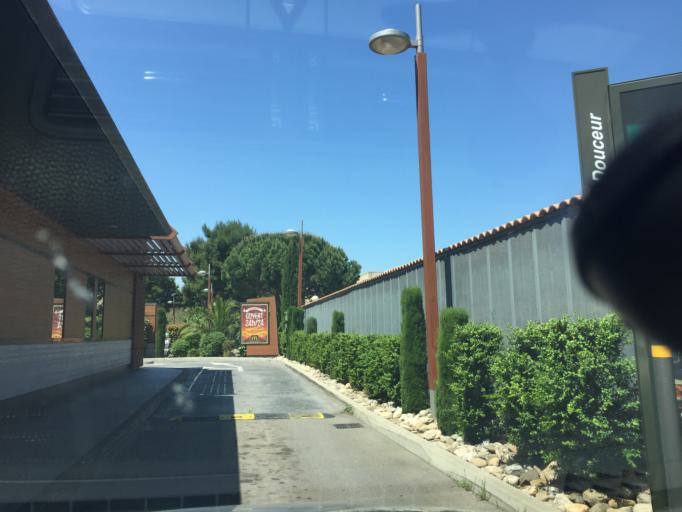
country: FR
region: Languedoc-Roussillon
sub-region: Departement de l'Aude
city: Narbonne
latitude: 43.1817
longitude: 3.0281
